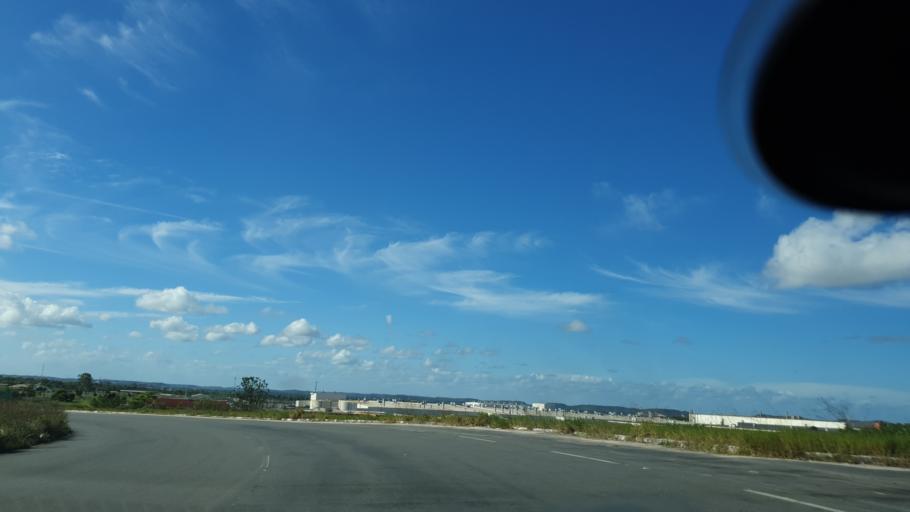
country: BR
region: Bahia
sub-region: Camacari
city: Camacari
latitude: -12.6798
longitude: -38.2816
